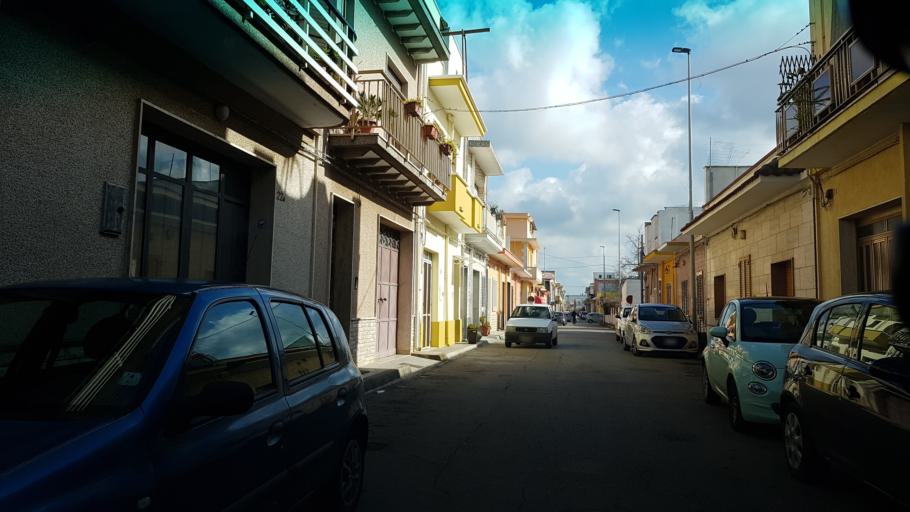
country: IT
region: Apulia
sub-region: Provincia di Brindisi
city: San Pietro Vernotico
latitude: 40.4816
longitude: 17.9977
